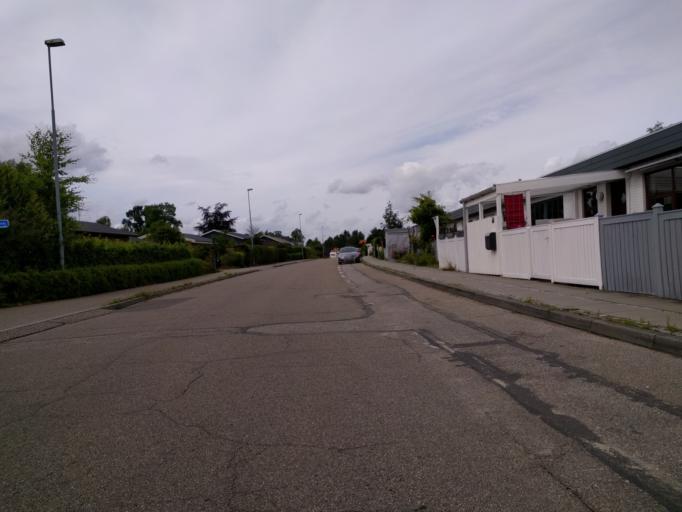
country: DK
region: Central Jutland
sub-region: Skanderborg Kommune
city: Ry
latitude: 56.0817
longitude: 9.7663
